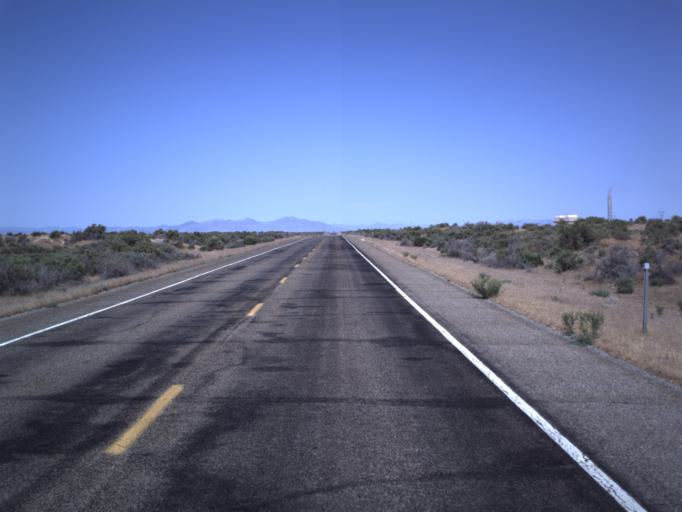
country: US
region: Utah
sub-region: Millard County
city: Delta
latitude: 39.4831
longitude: -112.5225
